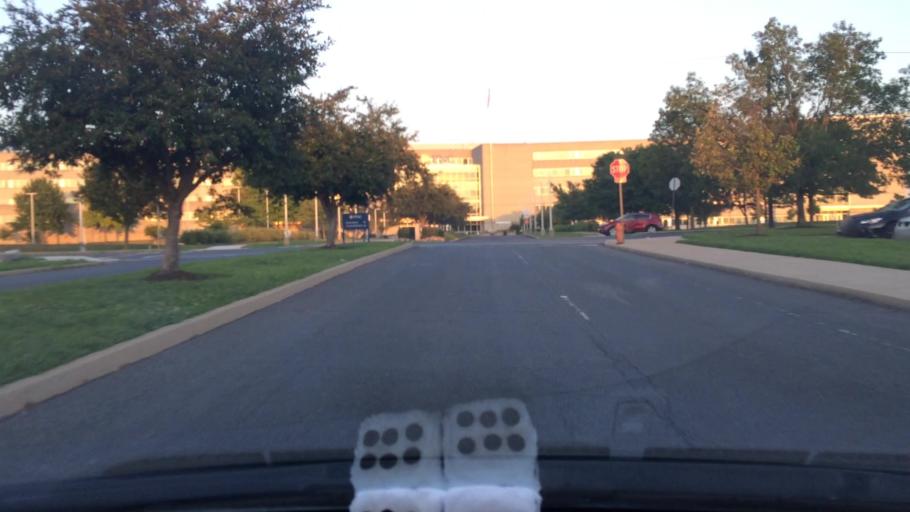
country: US
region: Pennsylvania
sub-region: Delaware County
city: Colwyn
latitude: 39.8871
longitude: -75.2472
